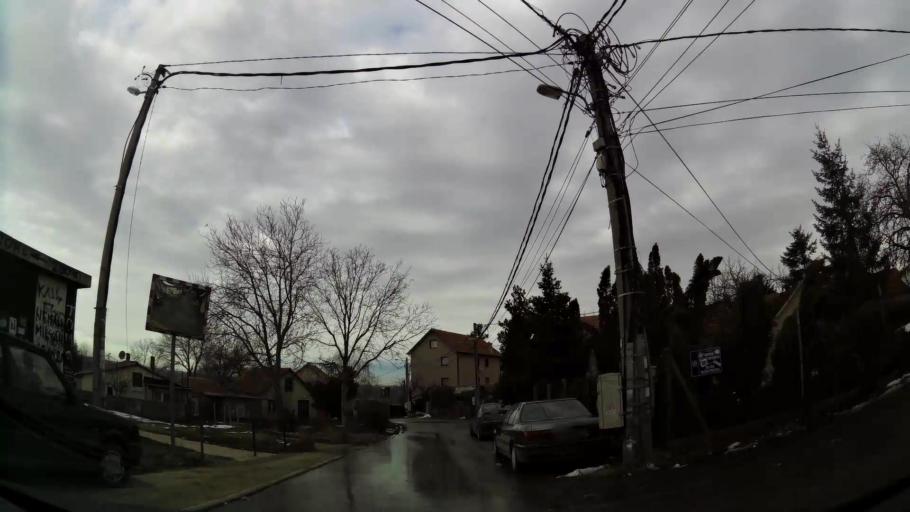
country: RS
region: Central Serbia
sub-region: Belgrade
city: Cukarica
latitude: 44.7443
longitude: 20.3964
